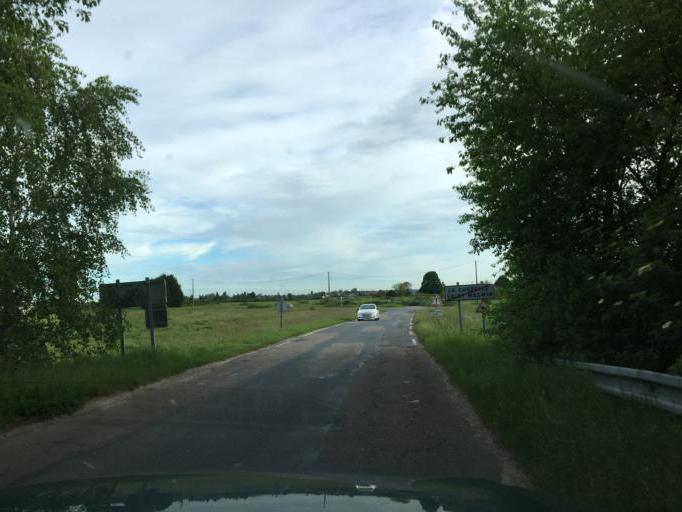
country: FR
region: Centre
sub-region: Departement du Loiret
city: Ingre
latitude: 47.9008
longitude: 1.8092
